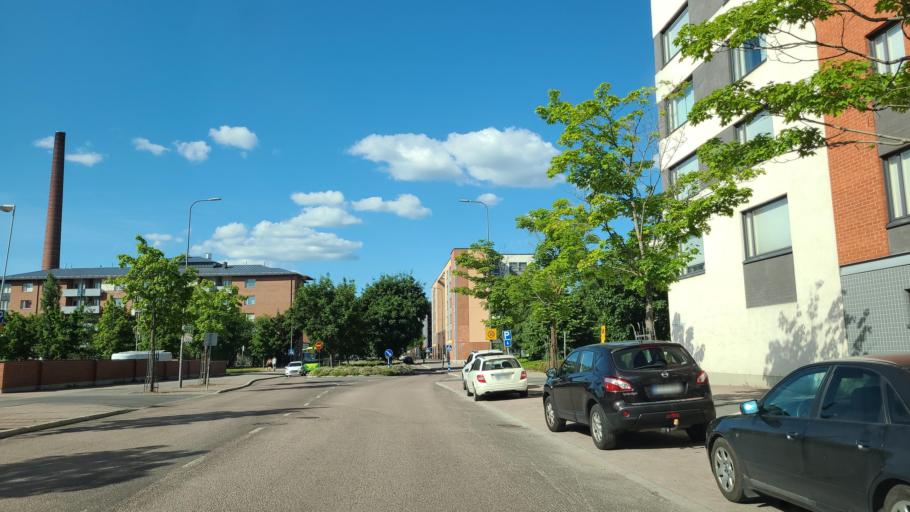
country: FI
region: Central Finland
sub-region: Jyvaeskylae
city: Jyvaeskylae
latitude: 62.2391
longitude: 25.7611
